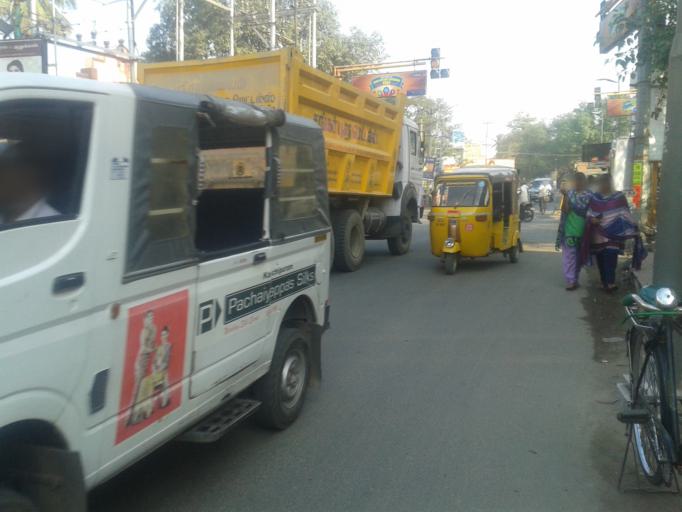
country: IN
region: Tamil Nadu
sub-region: Kancheepuram
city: Kanchipuram
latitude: 12.8244
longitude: 79.7102
